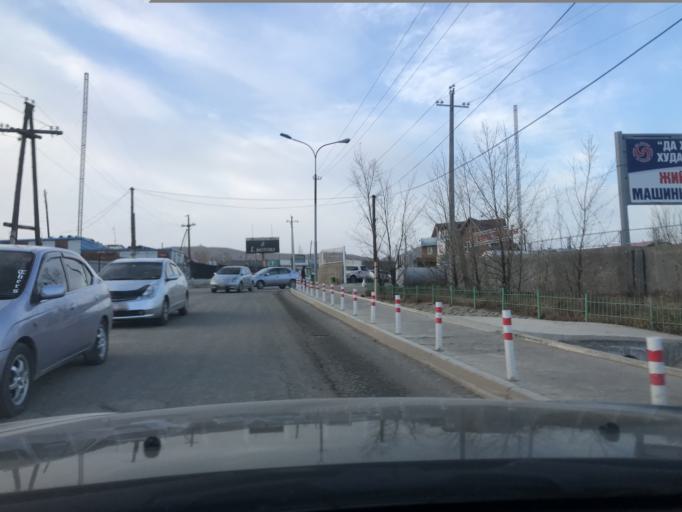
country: MN
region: Ulaanbaatar
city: Ulaanbaatar
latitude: 47.9290
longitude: 106.9976
